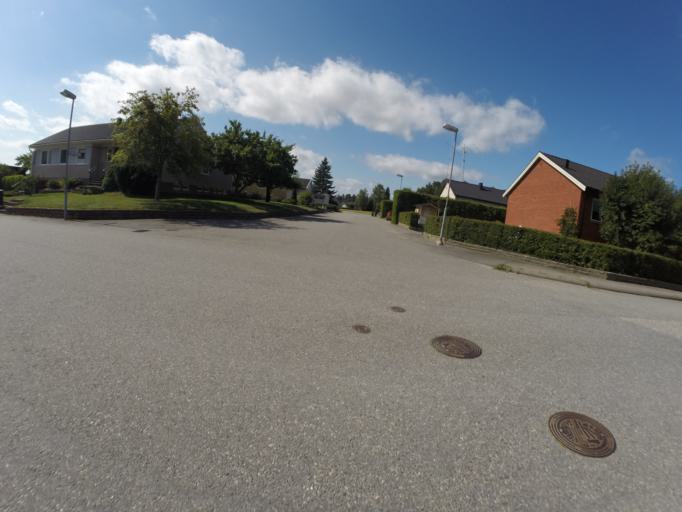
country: SE
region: Soedermanland
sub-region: Eskilstuna Kommun
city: Torshalla
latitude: 59.4122
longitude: 16.4871
